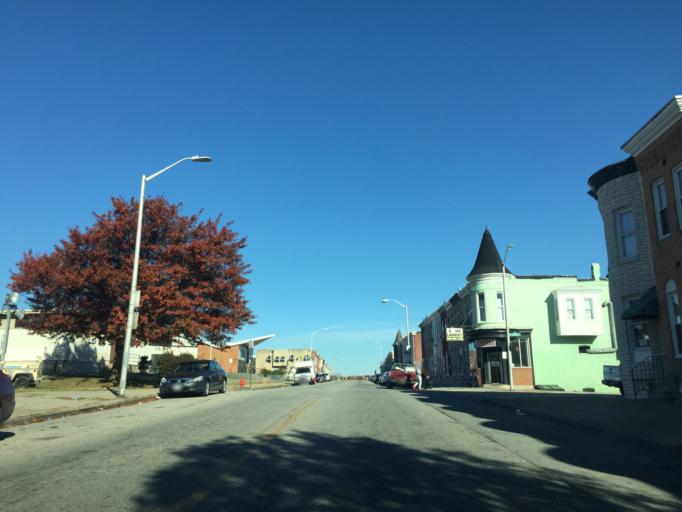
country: US
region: Maryland
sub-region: City of Baltimore
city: Baltimore
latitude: 39.3064
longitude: -76.5856
